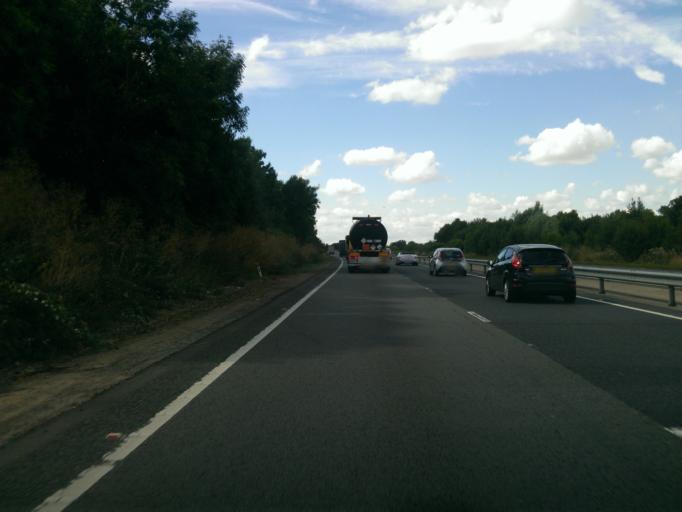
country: GB
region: England
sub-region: Bedford
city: Pertenhall
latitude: 52.3414
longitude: -0.3379
